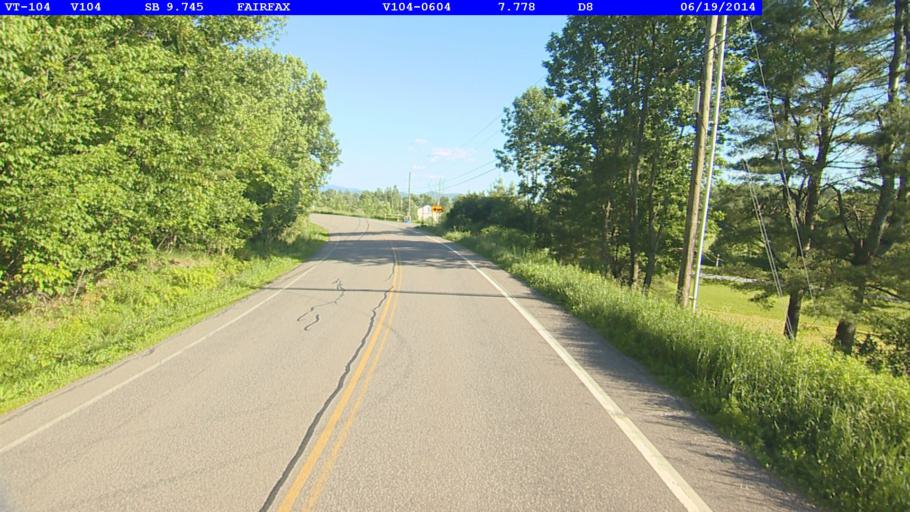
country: US
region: Vermont
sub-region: Chittenden County
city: Milton
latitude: 44.6965
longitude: -73.0370
